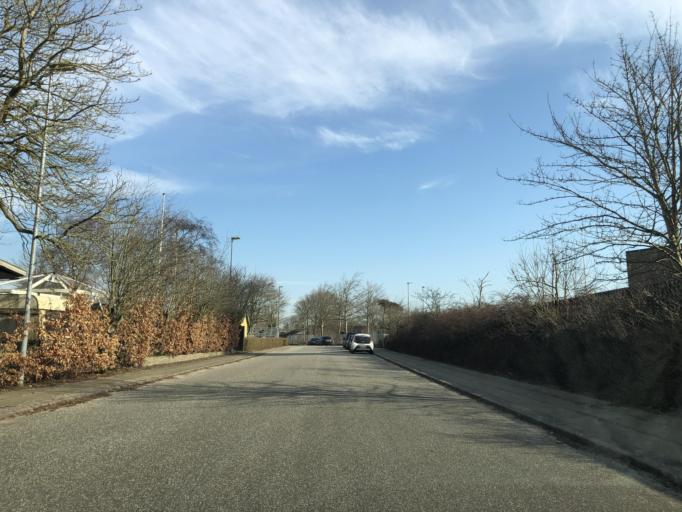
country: DK
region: Central Jutland
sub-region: Holstebro Kommune
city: Holstebro
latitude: 56.3502
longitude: 8.6101
